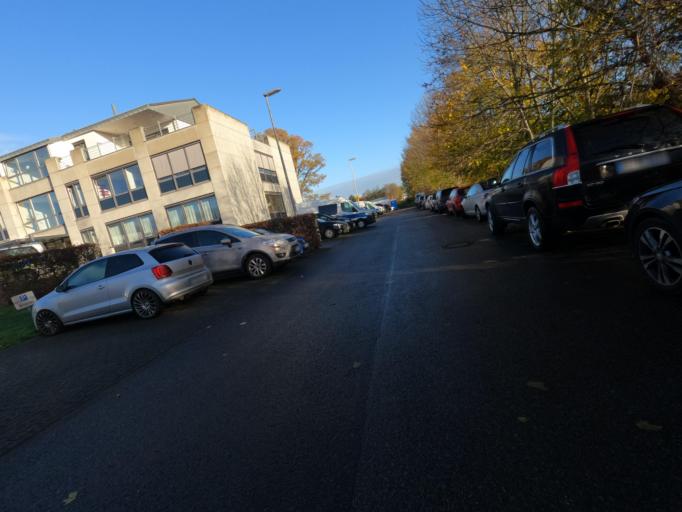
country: DE
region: North Rhine-Westphalia
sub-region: Regierungsbezirk Koln
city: Heinsberg
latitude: 51.0577
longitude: 6.1092
